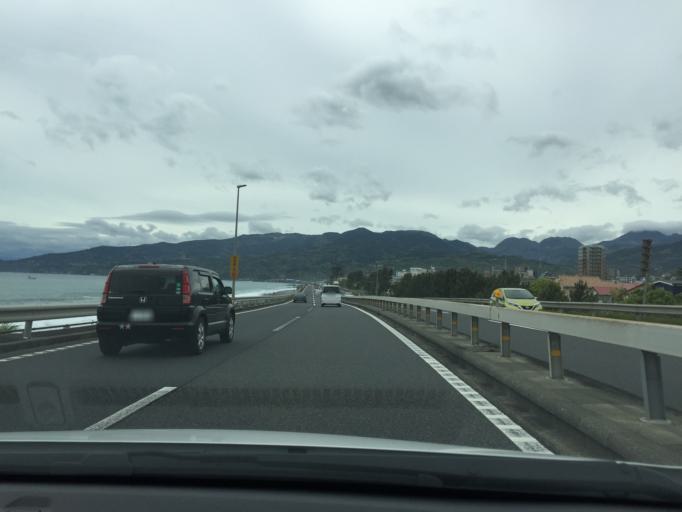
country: JP
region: Kanagawa
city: Odawara
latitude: 35.2543
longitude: 139.1708
